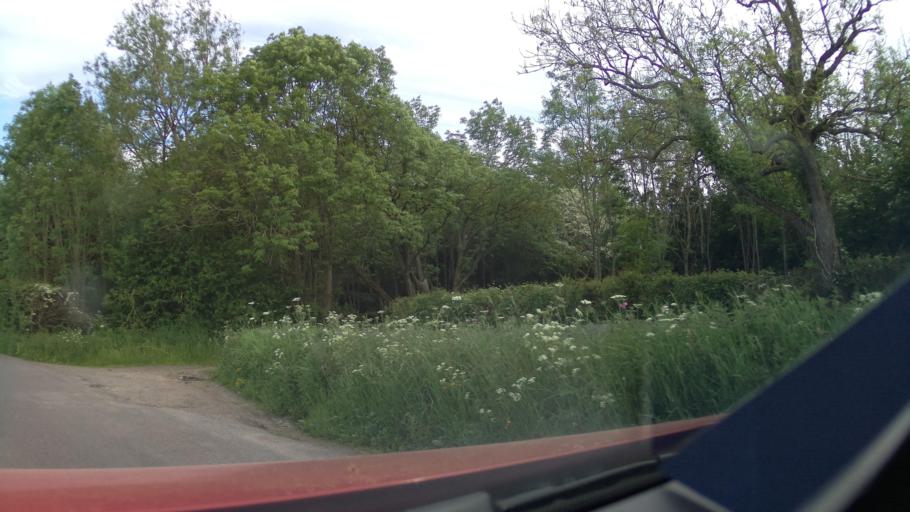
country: GB
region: England
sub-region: Gloucestershire
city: Chipping Campden
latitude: 52.0432
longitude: -1.7394
